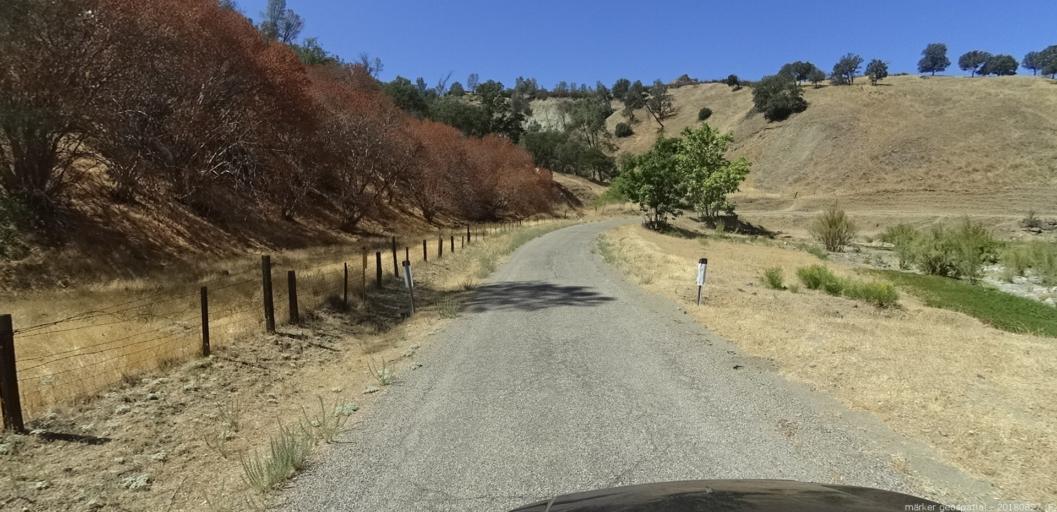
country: US
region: California
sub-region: Monterey County
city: King City
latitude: 36.2846
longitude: -120.8557
